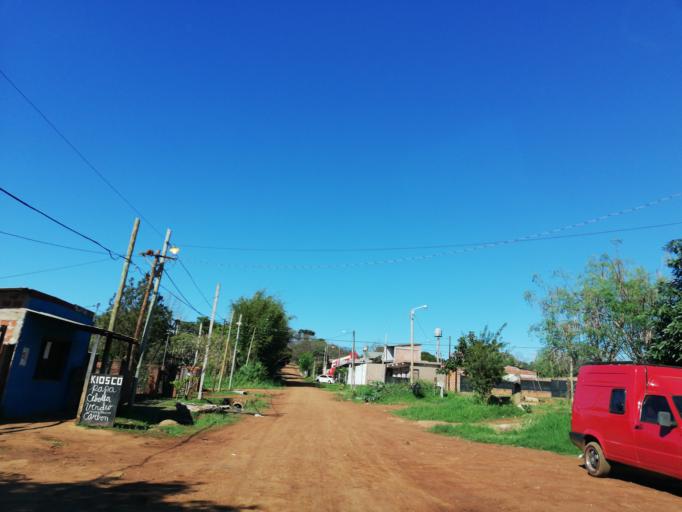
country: AR
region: Misiones
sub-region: Departamento de Capital
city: Posadas
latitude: -27.3949
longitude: -55.9299
